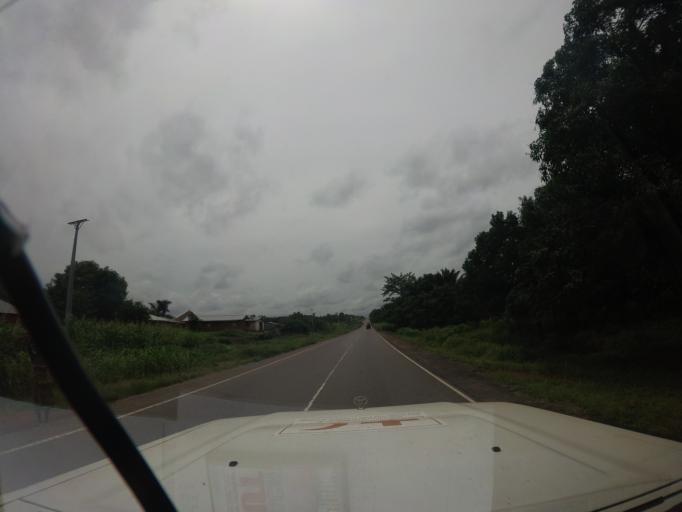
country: SL
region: Northern Province
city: Magburaka
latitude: 8.6863
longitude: -11.9135
